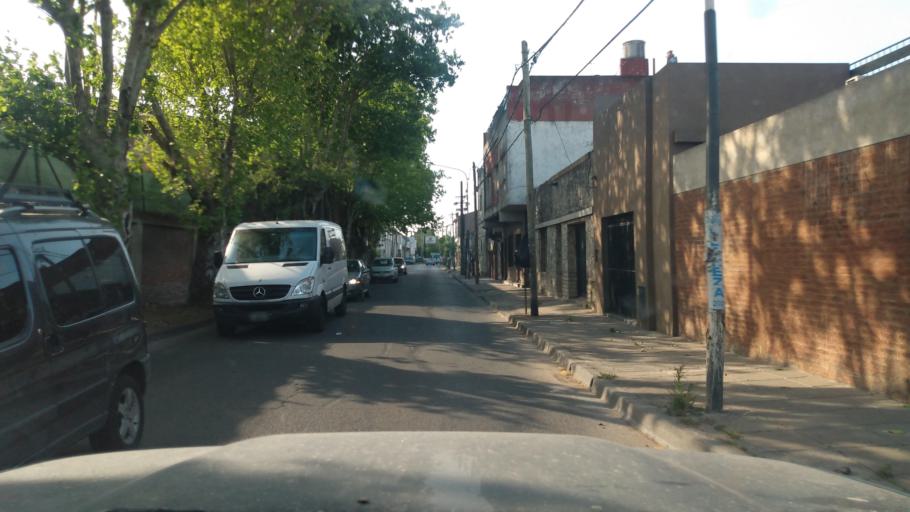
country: AR
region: Buenos Aires
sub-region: Partido de Moron
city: Moron
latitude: -34.6534
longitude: -58.6013
